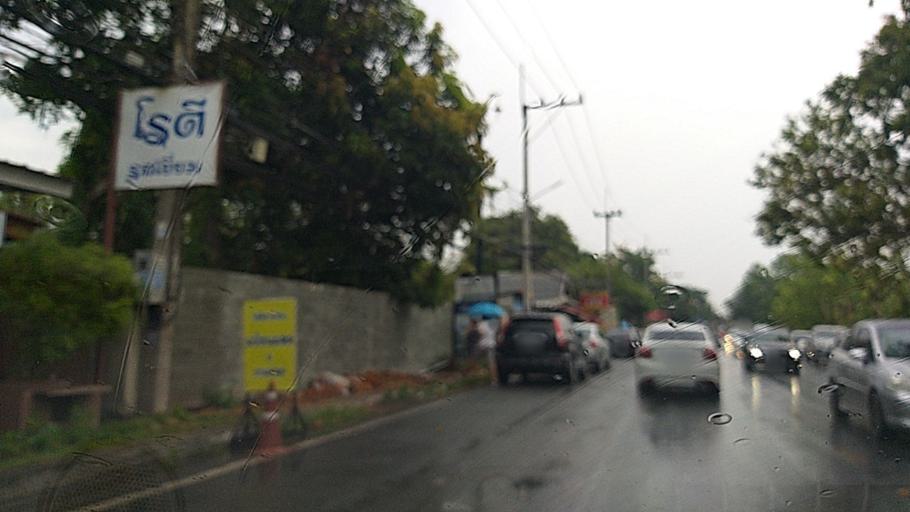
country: TH
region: Phra Nakhon Si Ayutthaya
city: Phra Nakhon Si Ayutthaya
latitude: 14.3407
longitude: 100.5530
